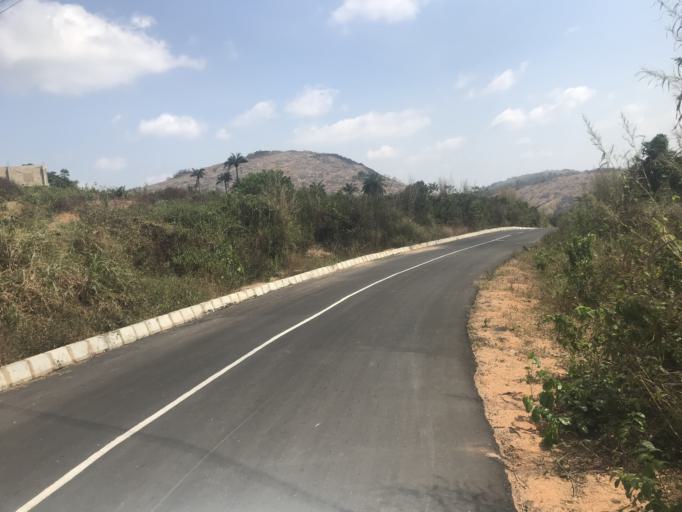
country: NG
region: Osun
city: Otan Ayegbaju
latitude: 7.9060
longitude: 4.8252
